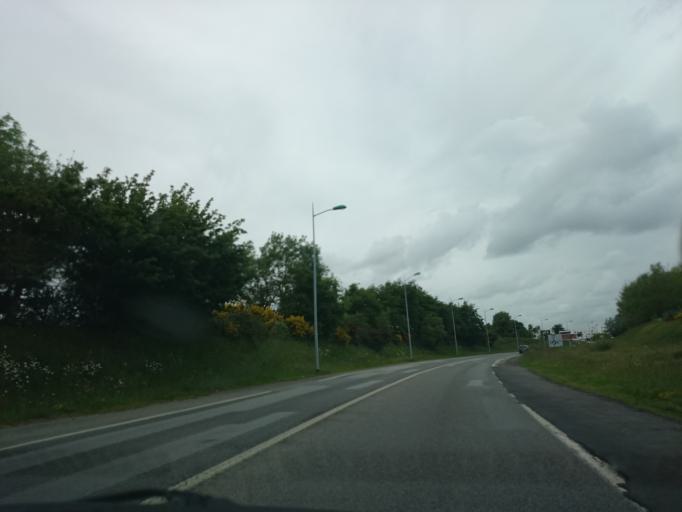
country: FR
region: Brittany
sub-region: Departement du Morbihan
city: Vannes
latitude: 47.6739
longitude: -2.7742
